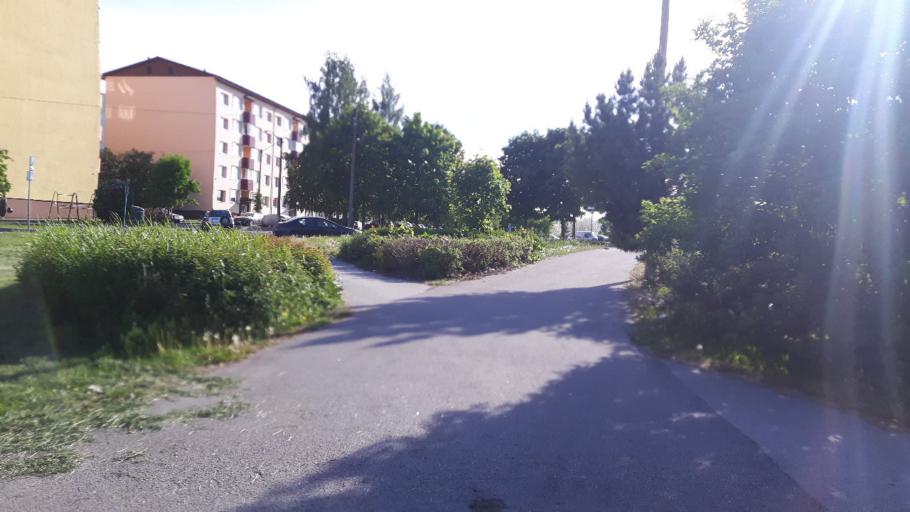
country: EE
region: Harju
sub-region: Tallinna linn
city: Kose
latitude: 59.4538
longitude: 24.8623
